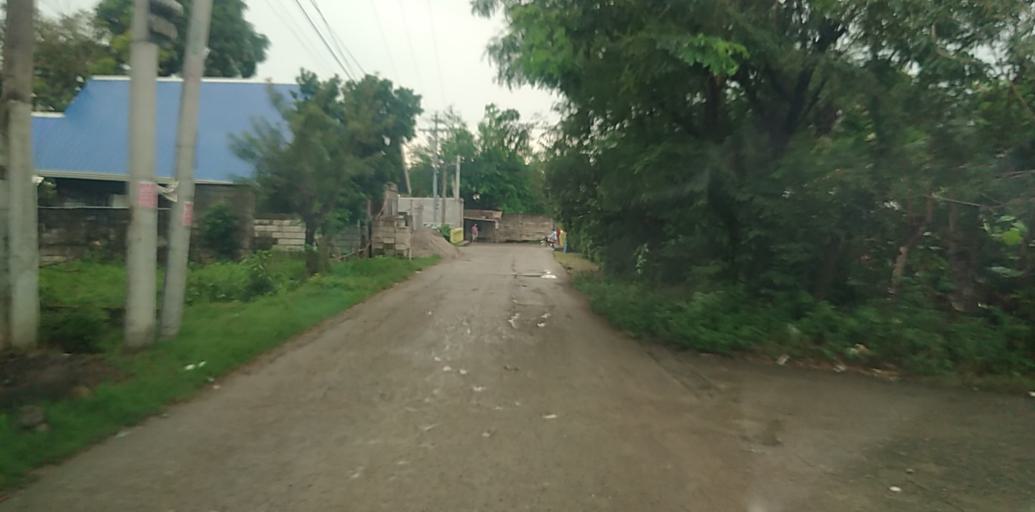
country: PH
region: Central Luzon
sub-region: Province of Pampanga
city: Arayat
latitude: 15.1507
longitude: 120.7478
